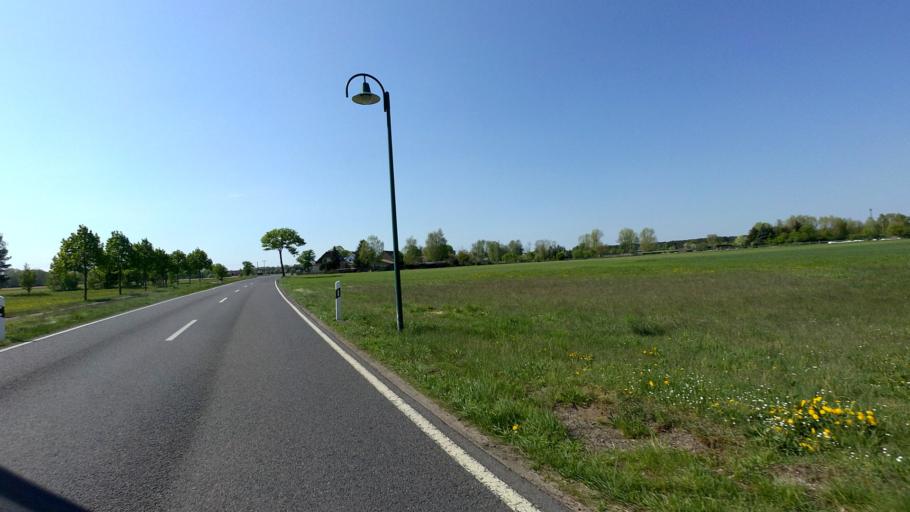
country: DE
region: Brandenburg
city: Schlepzig
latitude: 52.0550
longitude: 13.9684
